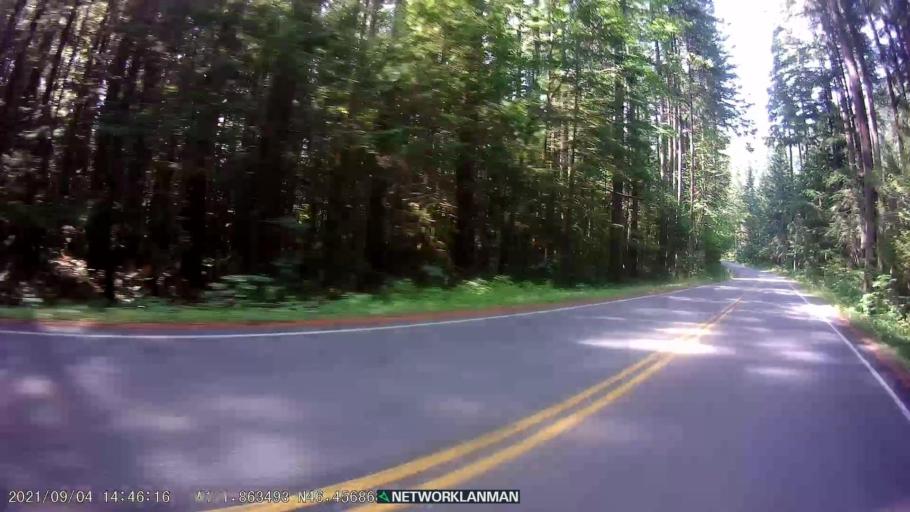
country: US
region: Washington
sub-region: Lewis County
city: Morton
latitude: 46.4572
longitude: -121.8634
